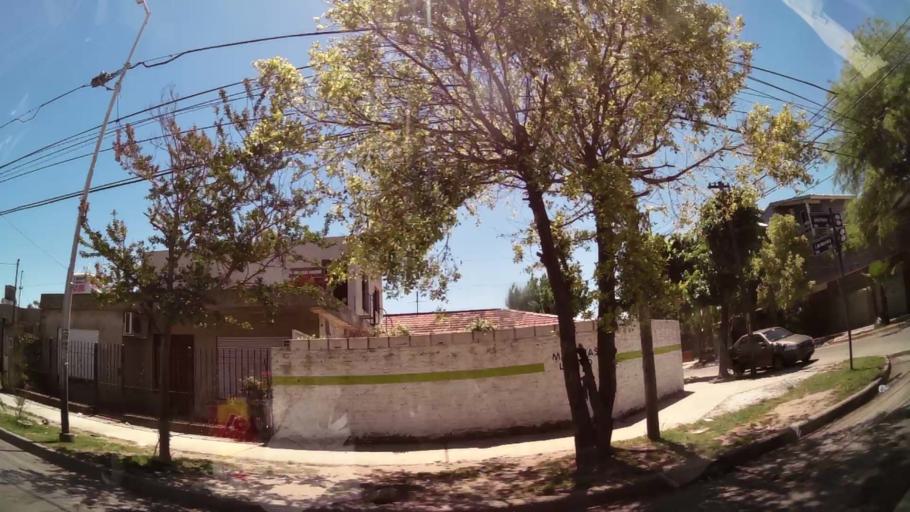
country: AR
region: Buenos Aires
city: Hurlingham
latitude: -34.4935
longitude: -58.6708
